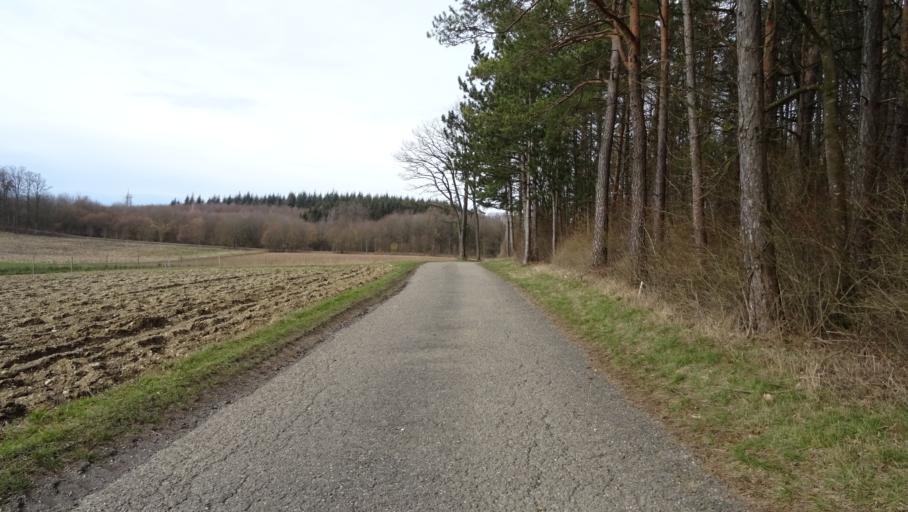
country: DE
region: Baden-Wuerttemberg
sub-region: Karlsruhe Region
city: Limbach
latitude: 49.4352
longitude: 9.2677
